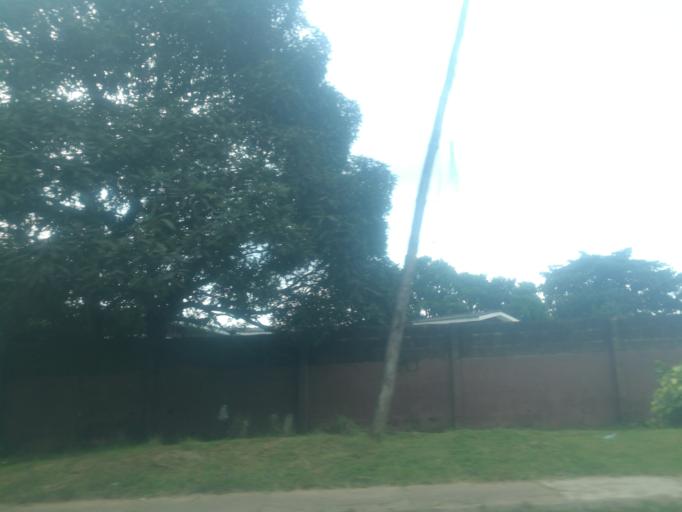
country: NG
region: Oyo
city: Ibadan
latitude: 7.4482
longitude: 3.9015
